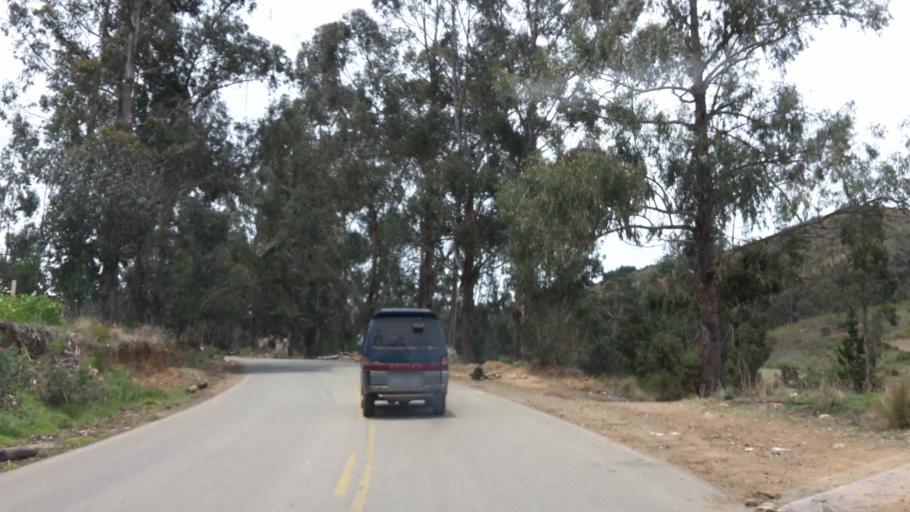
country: BO
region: Cochabamba
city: Totora
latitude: -17.7186
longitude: -65.2042
